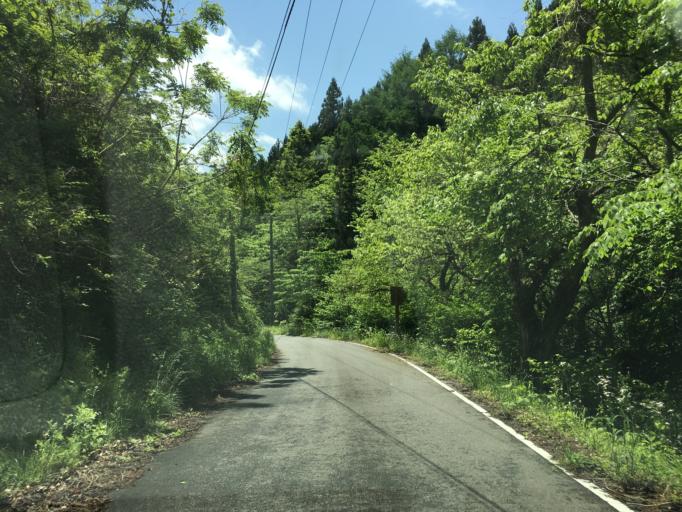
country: JP
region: Miyagi
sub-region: Oshika Gun
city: Onagawa Cho
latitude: 38.6748
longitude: 141.3468
